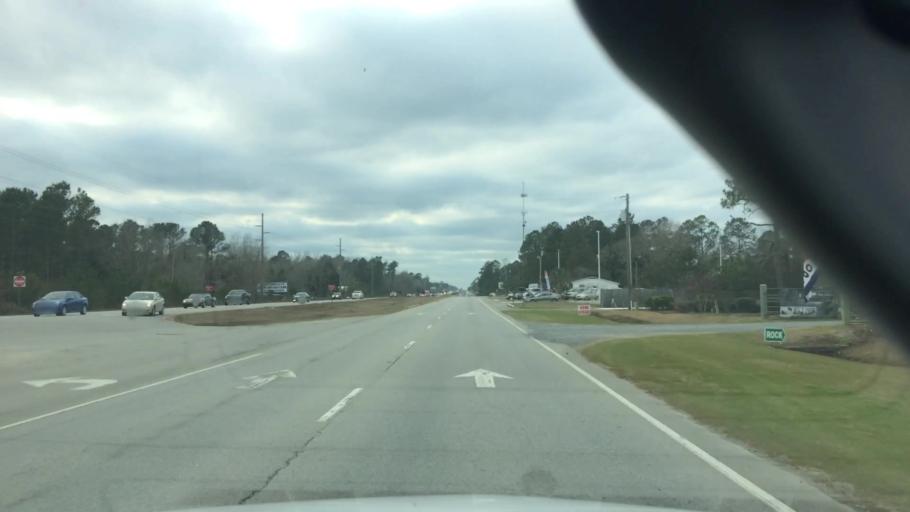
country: US
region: North Carolina
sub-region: Brunswick County
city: Sunset Beach
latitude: 33.9494
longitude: -78.4837
